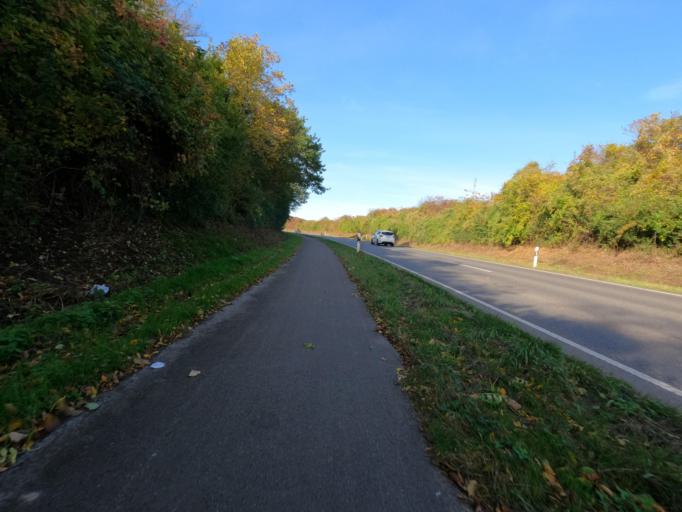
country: DE
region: North Rhine-Westphalia
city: Huckelhoven
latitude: 51.0361
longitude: 6.2764
